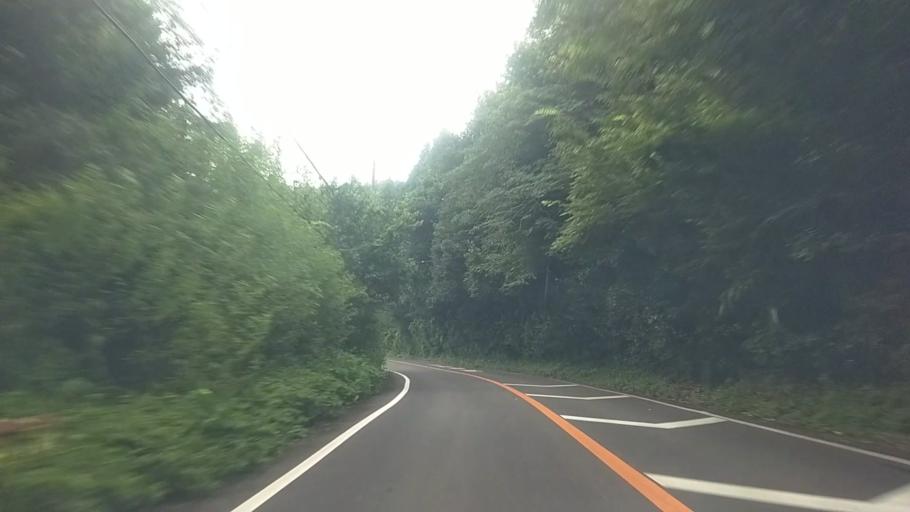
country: JP
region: Chiba
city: Kawaguchi
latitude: 35.2431
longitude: 140.0737
